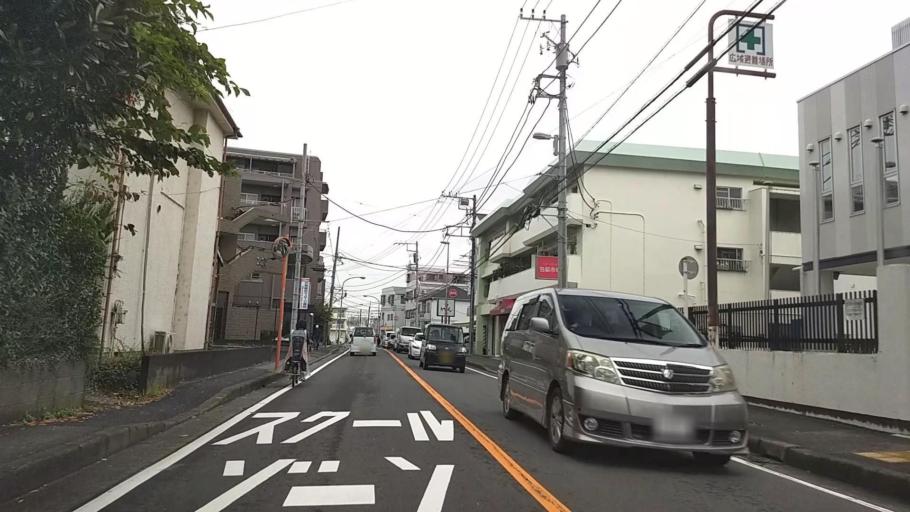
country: JP
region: Kanagawa
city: Fujisawa
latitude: 35.3973
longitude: 139.5361
